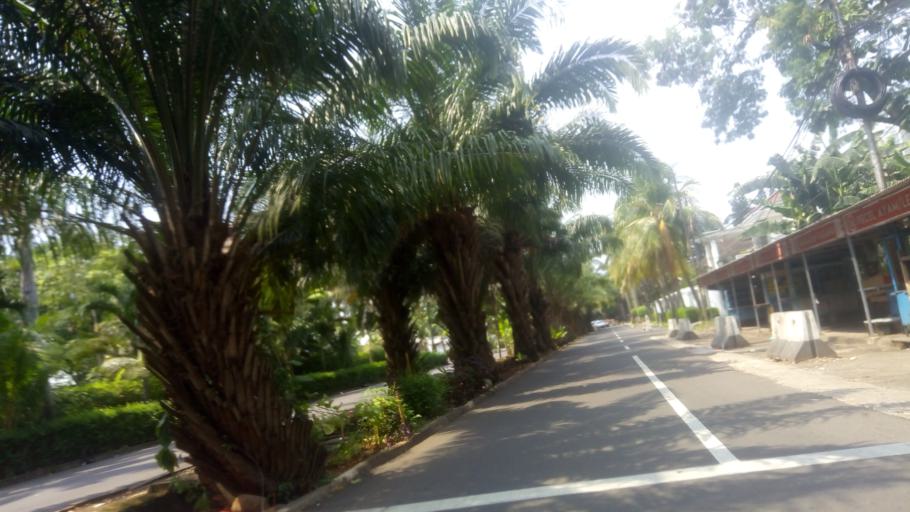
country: ID
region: Jakarta Raya
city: Jakarta
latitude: -6.2347
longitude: 106.8319
